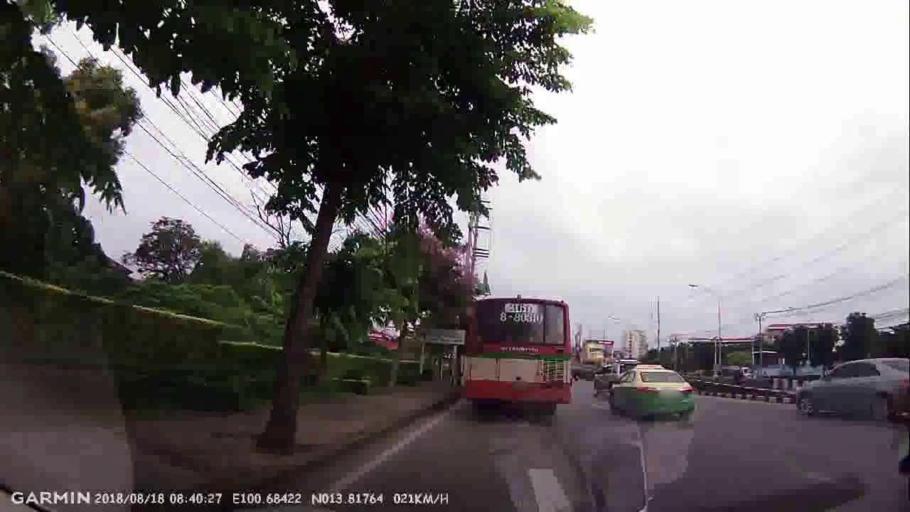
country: TH
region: Bangkok
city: Khan Na Yao
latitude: 13.8177
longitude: 100.6842
